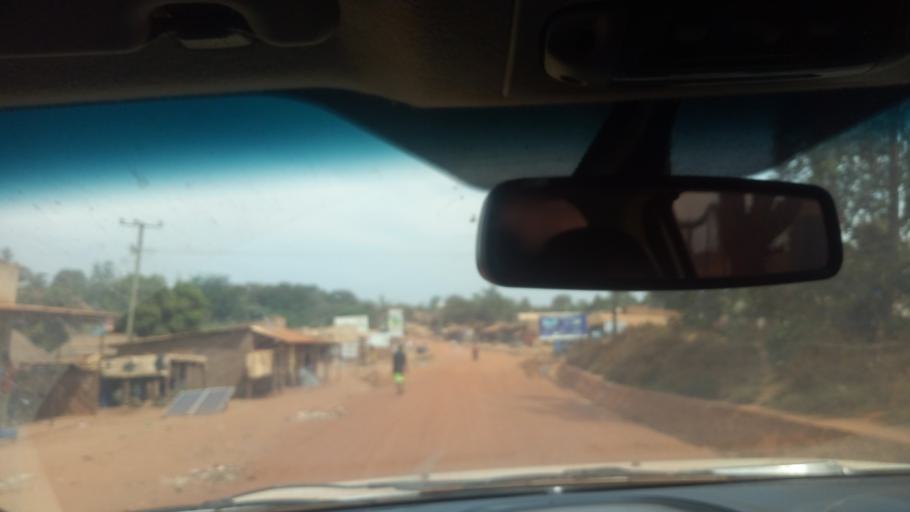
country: UG
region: Western Region
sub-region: Kiryandongo District
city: Kiryandongo
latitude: 1.9405
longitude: 32.1647
